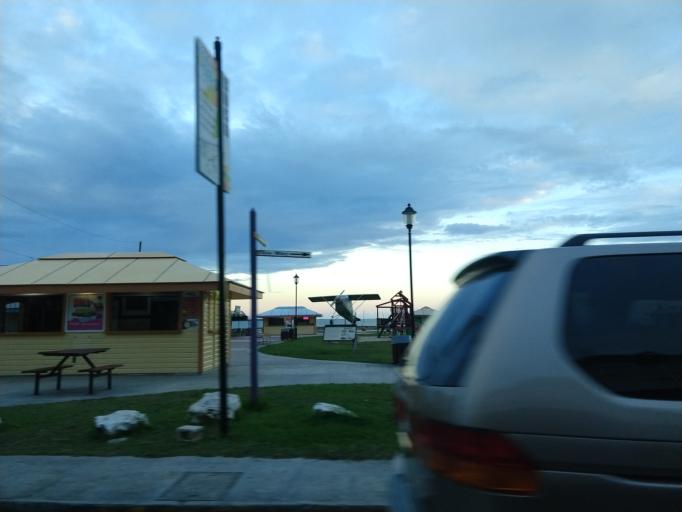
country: BZ
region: Belize
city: Belize City
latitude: 17.5081
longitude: -88.1879
